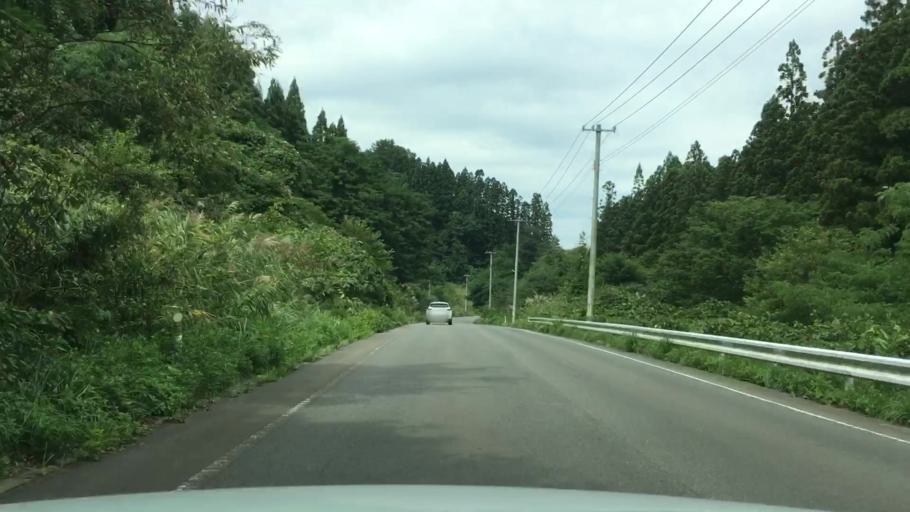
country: JP
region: Aomori
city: Shimokizukuri
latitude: 40.7428
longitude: 140.2432
